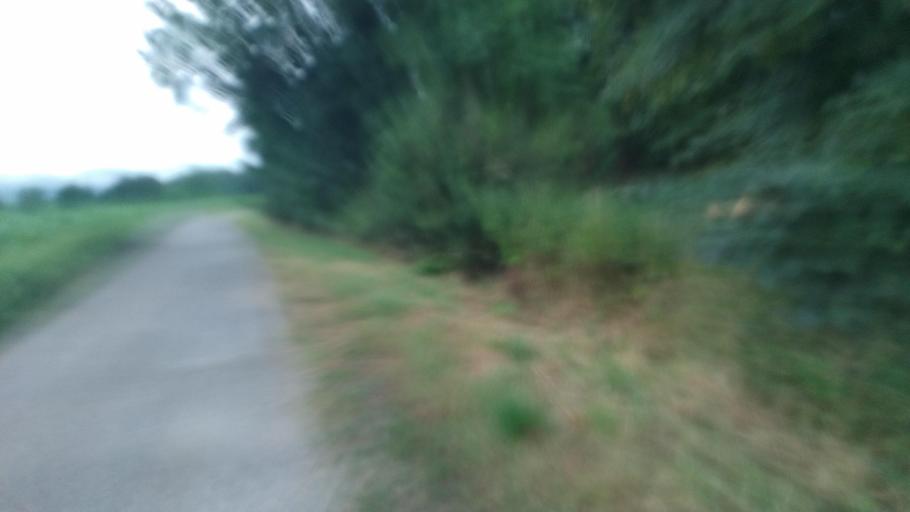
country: DE
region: Baden-Wuerttemberg
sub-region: Karlsruhe Region
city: Ettlingen
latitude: 48.9651
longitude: 8.3822
